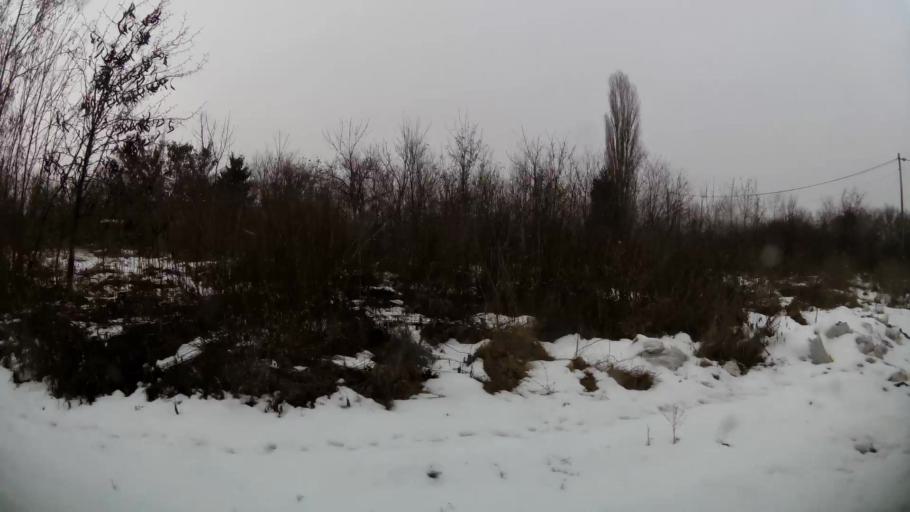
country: RO
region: Ilfov
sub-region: Comuna Mogosoaia
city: Mogosoaia
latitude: 44.5128
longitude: 26.0278
